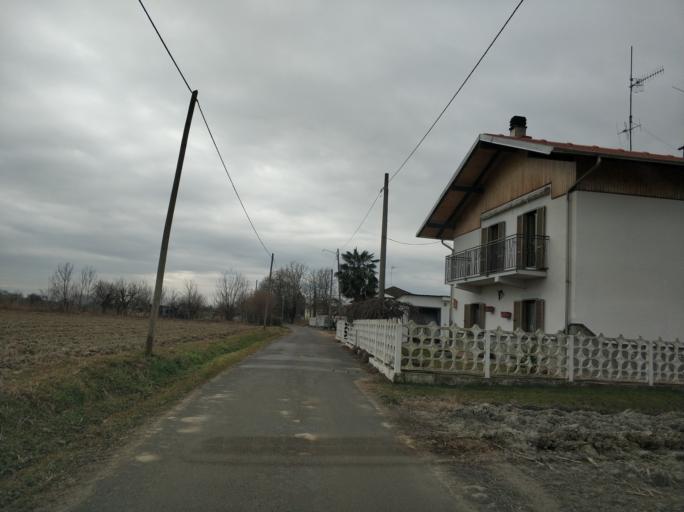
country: IT
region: Piedmont
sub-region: Provincia di Torino
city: Ivrea
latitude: 45.4462
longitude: 7.8836
